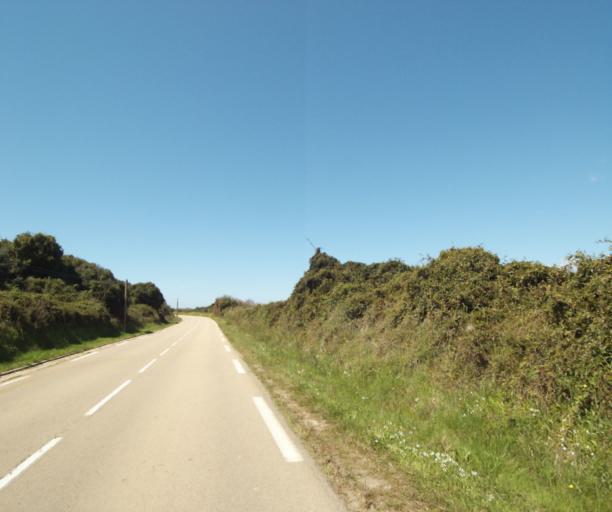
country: FR
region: Corsica
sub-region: Departement de la Corse-du-Sud
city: Propriano
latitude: 41.6536
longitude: 8.8879
